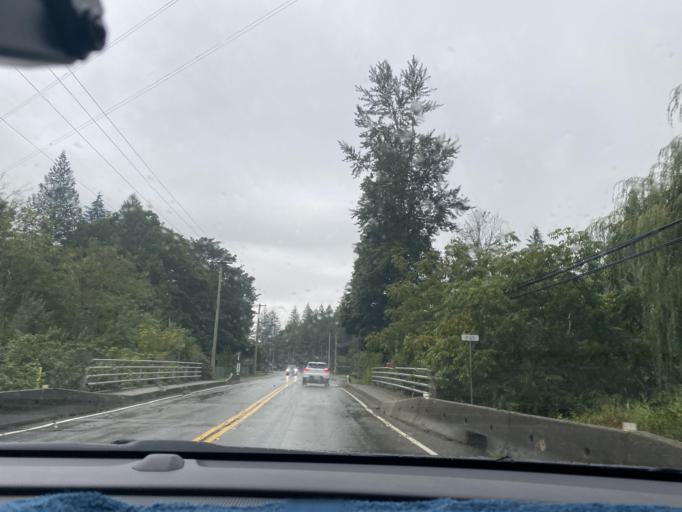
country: CA
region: British Columbia
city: Agassiz
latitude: 49.2834
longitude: -121.7817
